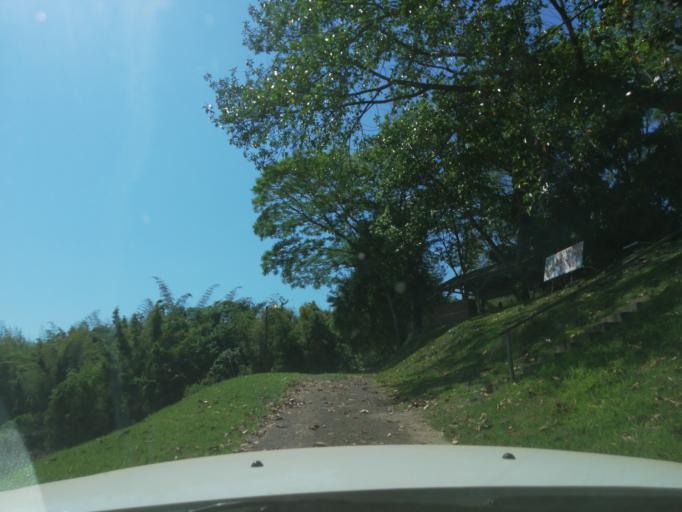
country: AR
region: Misiones
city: Puerto Leoni
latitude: -26.9584
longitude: -55.1522
